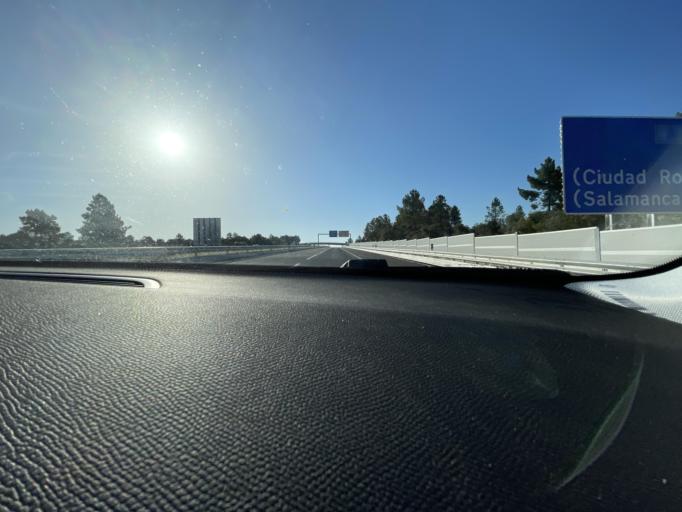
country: ES
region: Castille and Leon
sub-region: Provincia de Salamanca
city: Fuentes de Onoro
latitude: 40.6158
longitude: -6.8270
